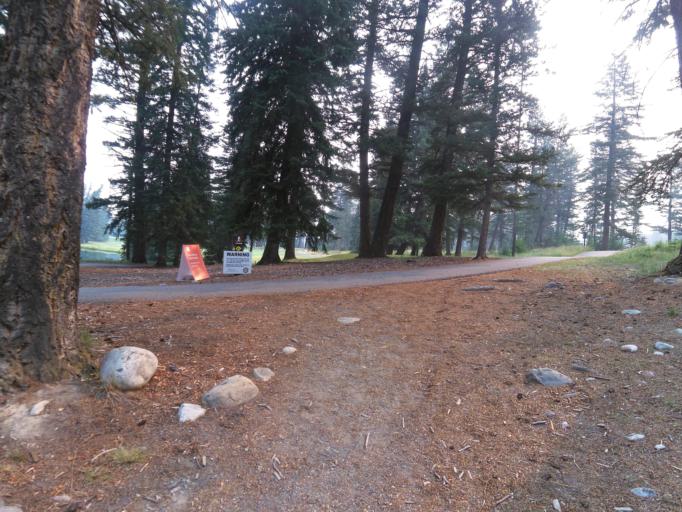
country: CA
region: Alberta
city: Jasper Park Lodge
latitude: 52.8786
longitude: -118.0595
